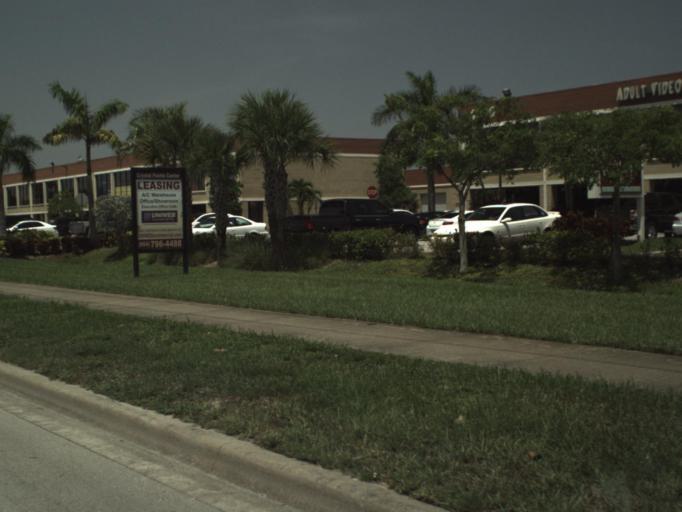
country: US
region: Florida
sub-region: Broward County
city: Tedder
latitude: 26.2855
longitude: -80.1523
